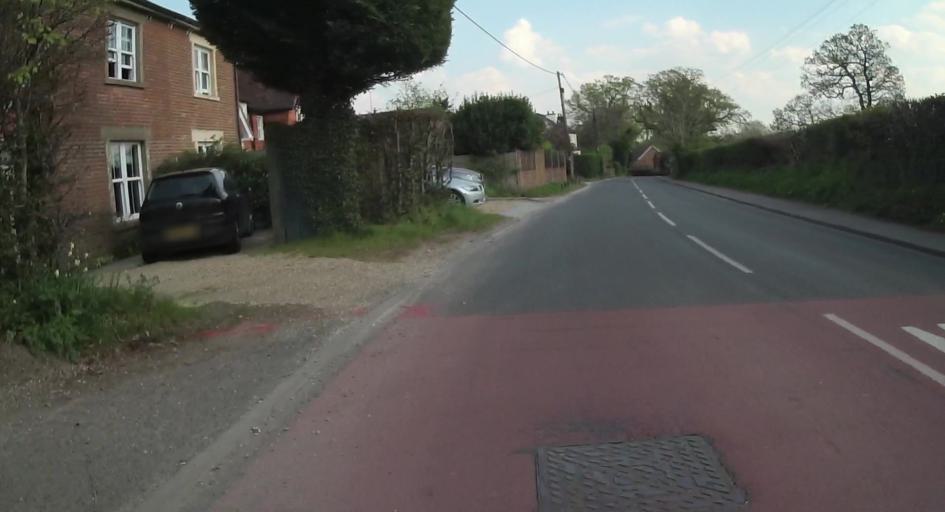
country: GB
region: England
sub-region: West Berkshire
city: Stratfield Mortimer
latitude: 51.3747
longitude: -1.0481
